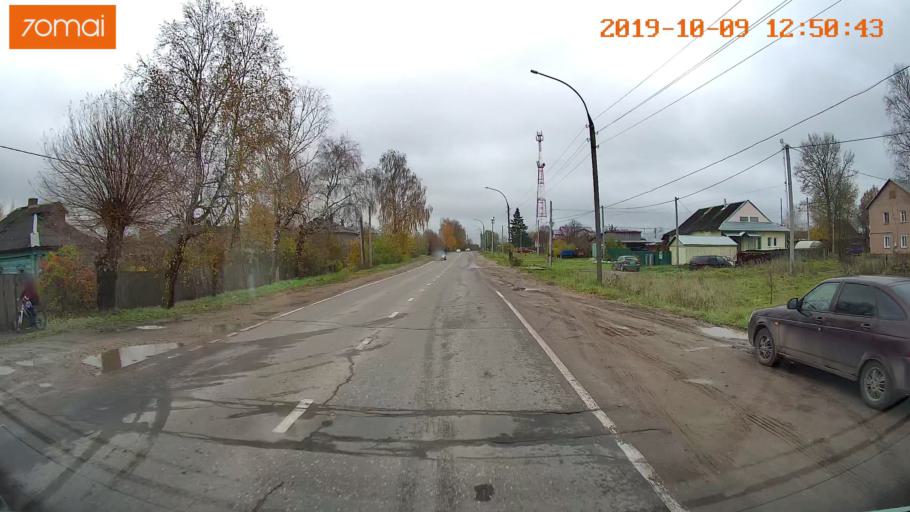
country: RU
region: Jaroslavl
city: Prechistoye
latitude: 58.4229
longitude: 40.3322
